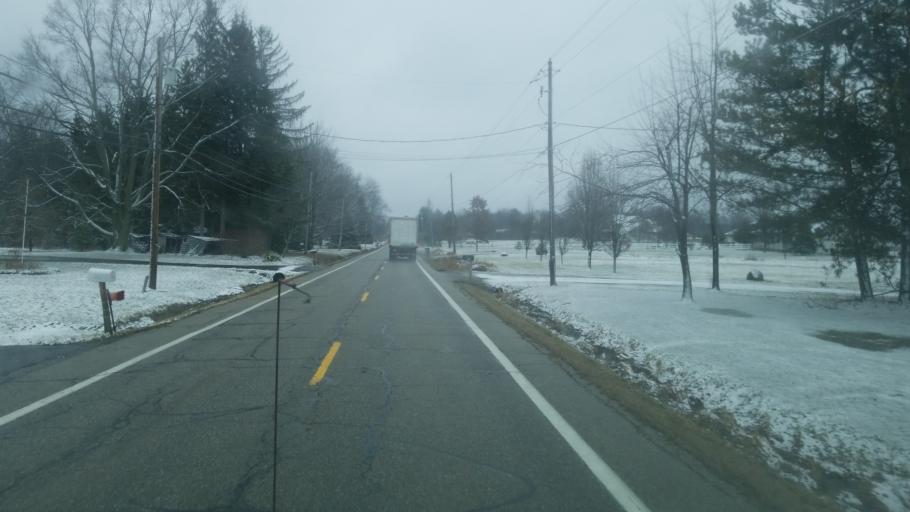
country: US
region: Ohio
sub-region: Portage County
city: Garrettsville
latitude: 41.2450
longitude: -81.1260
